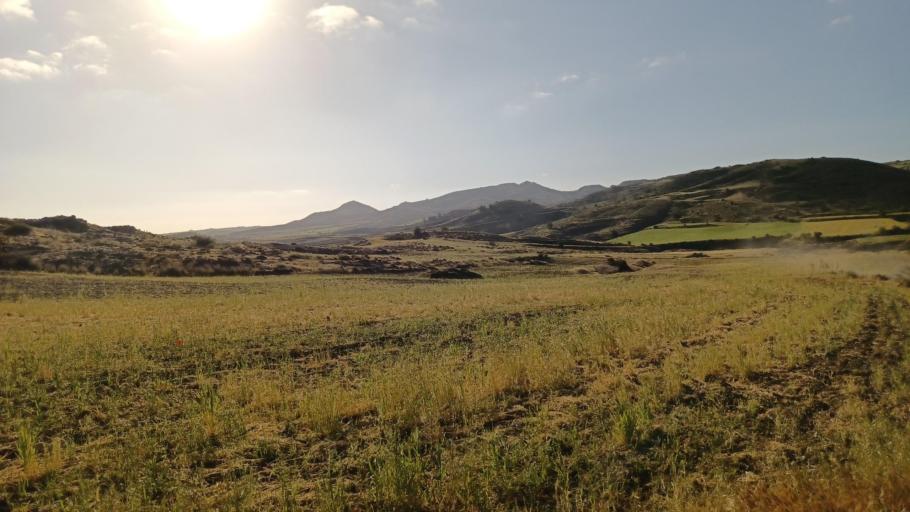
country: CY
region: Lefkosia
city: Peristerona
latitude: 35.0730
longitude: 33.0436
